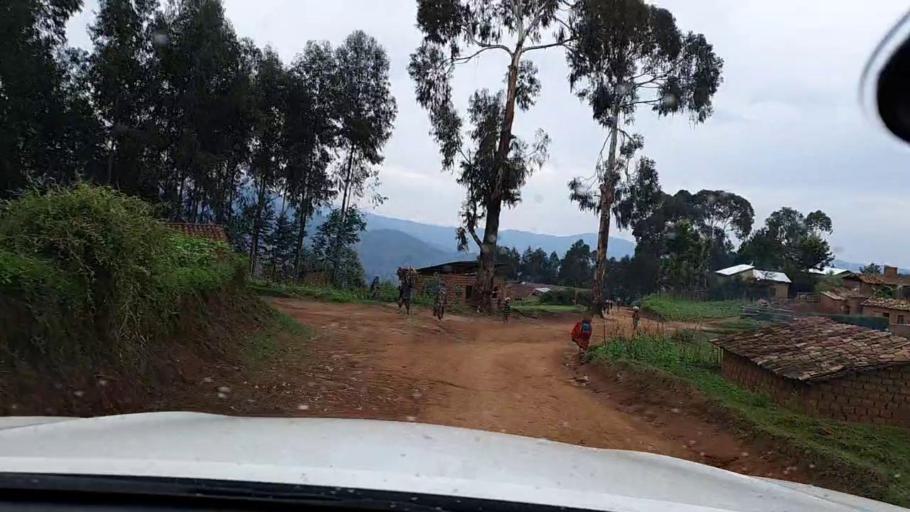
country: RW
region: Southern Province
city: Nzega
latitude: -2.3806
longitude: 29.2420
